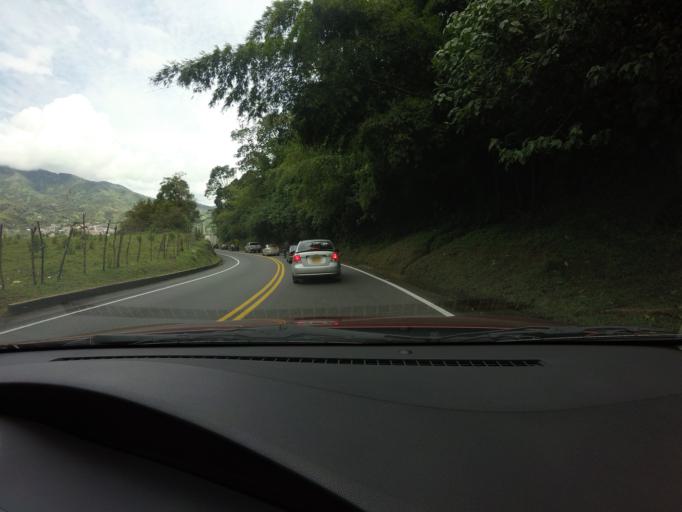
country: CO
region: Antioquia
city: Cocorna
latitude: 6.0353
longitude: -75.1885
